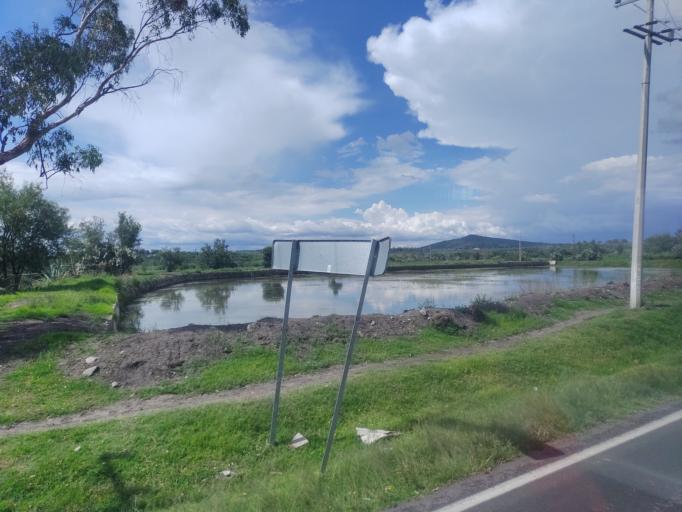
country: MX
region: Mexico
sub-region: Aculco
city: El Colorado
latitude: 20.0932
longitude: -99.7915
